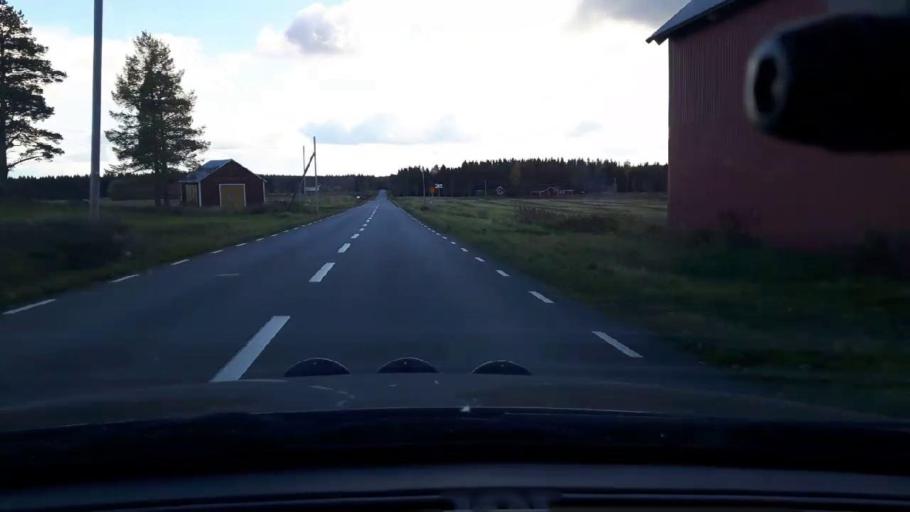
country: SE
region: Jaemtland
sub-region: Bergs Kommun
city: Hoverberg
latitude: 63.0639
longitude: 14.3283
